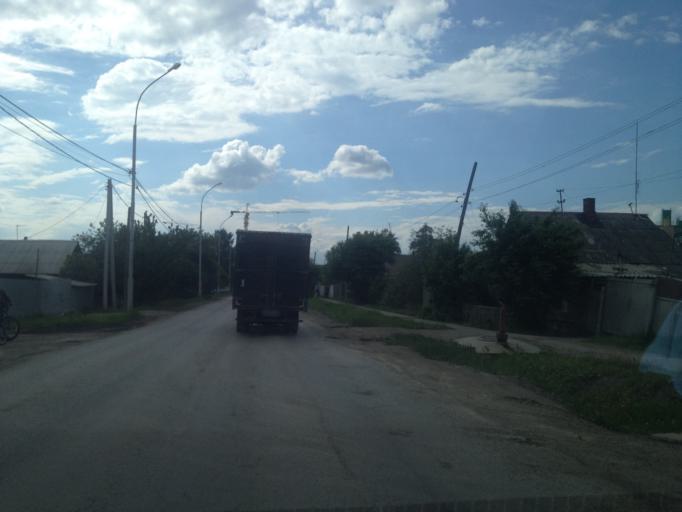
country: RU
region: Sverdlovsk
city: Sovkhoznyy
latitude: 56.7642
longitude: 60.5610
